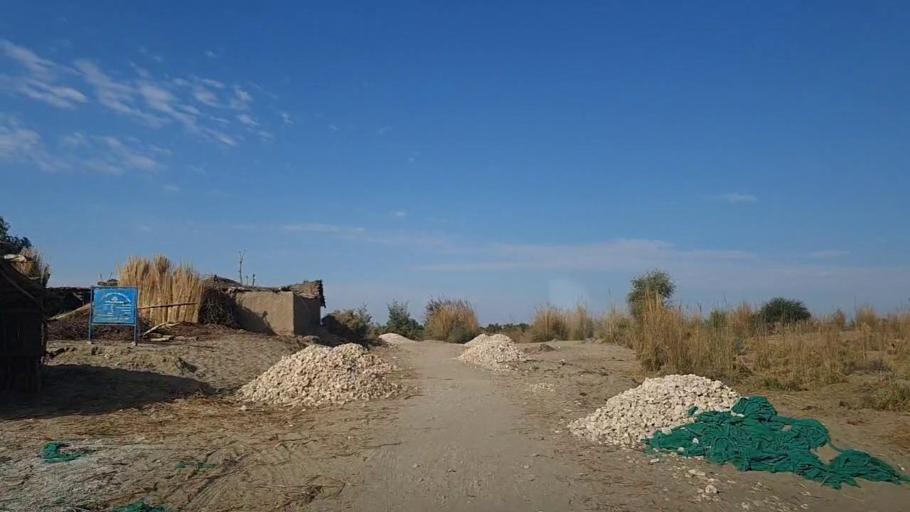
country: PK
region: Sindh
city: Jam Sahib
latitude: 26.3134
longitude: 68.8141
